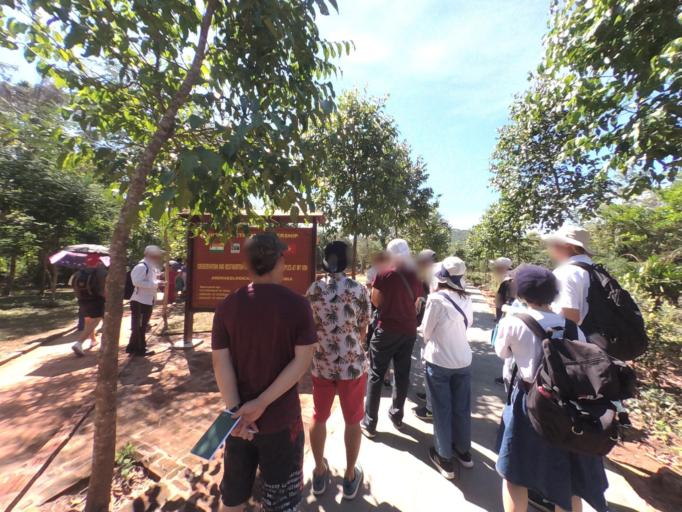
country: VN
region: Quang Nam
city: Dai Loc
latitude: 15.7679
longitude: 108.1208
